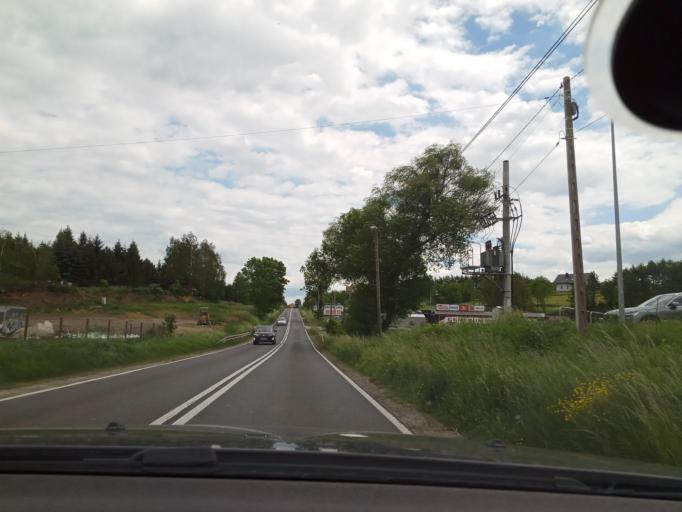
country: PL
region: Lesser Poland Voivodeship
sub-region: Powiat wielicki
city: Trabki
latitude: 49.9684
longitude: 20.1341
